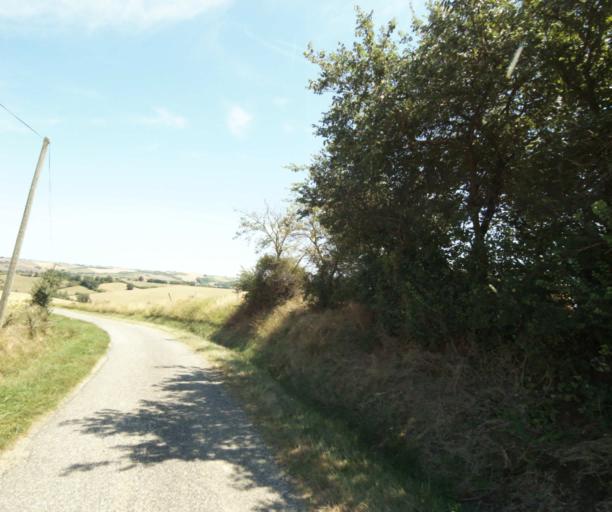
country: FR
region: Midi-Pyrenees
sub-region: Departement de l'Ariege
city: Lezat-sur-Leze
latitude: 43.2675
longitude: 1.3293
